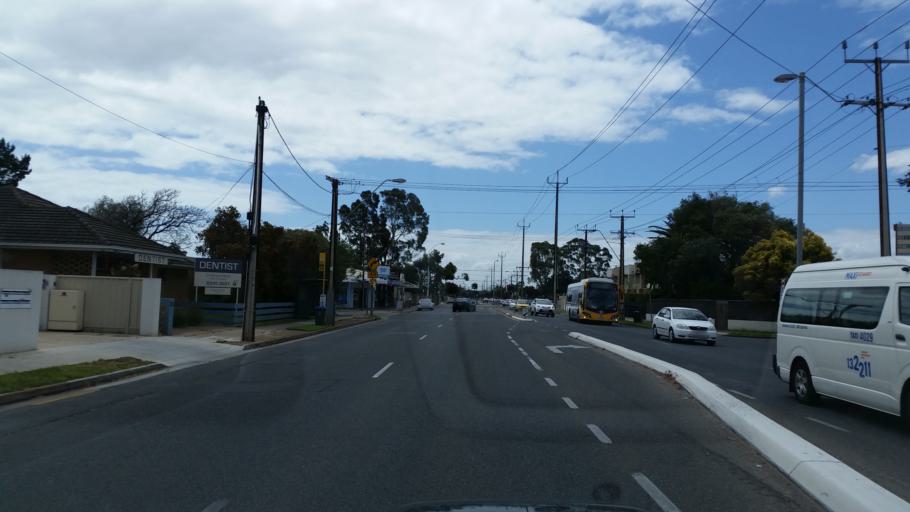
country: AU
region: South Australia
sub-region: Charles Sturt
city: Woodville West
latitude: -34.8867
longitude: 138.5312
